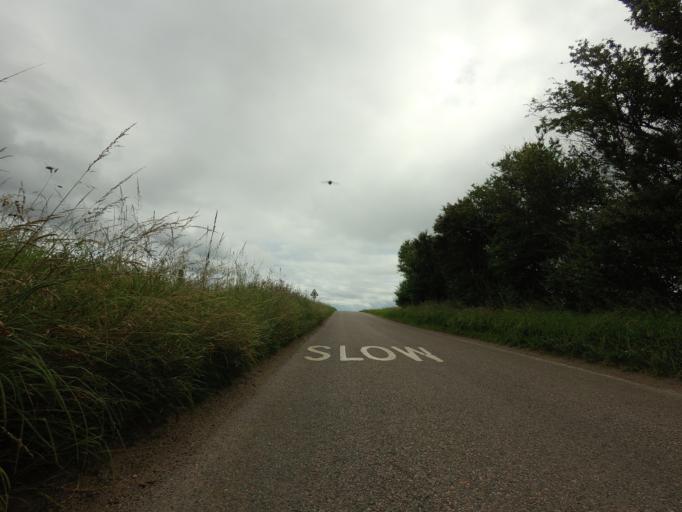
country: GB
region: Scotland
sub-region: Moray
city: Lhanbryd
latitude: 57.6599
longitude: -3.1938
